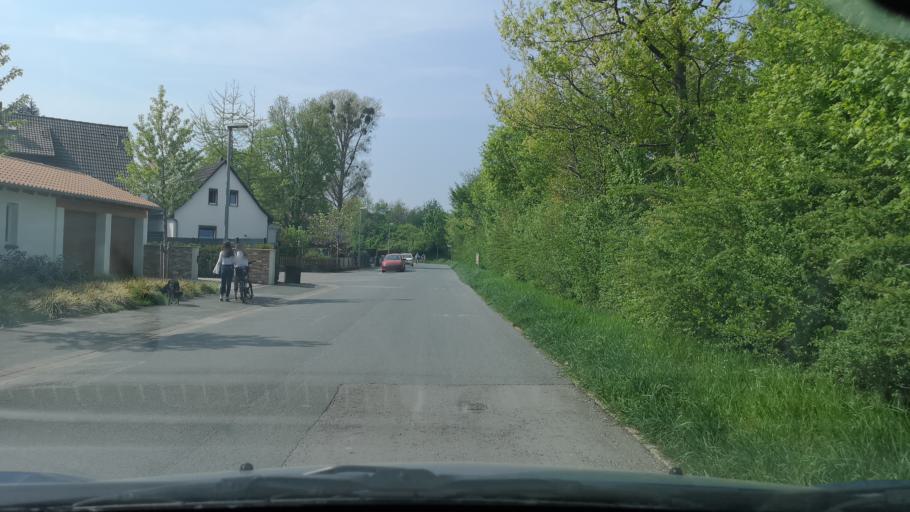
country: DE
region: Lower Saxony
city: Langenhagen
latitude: 52.4148
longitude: 9.7178
